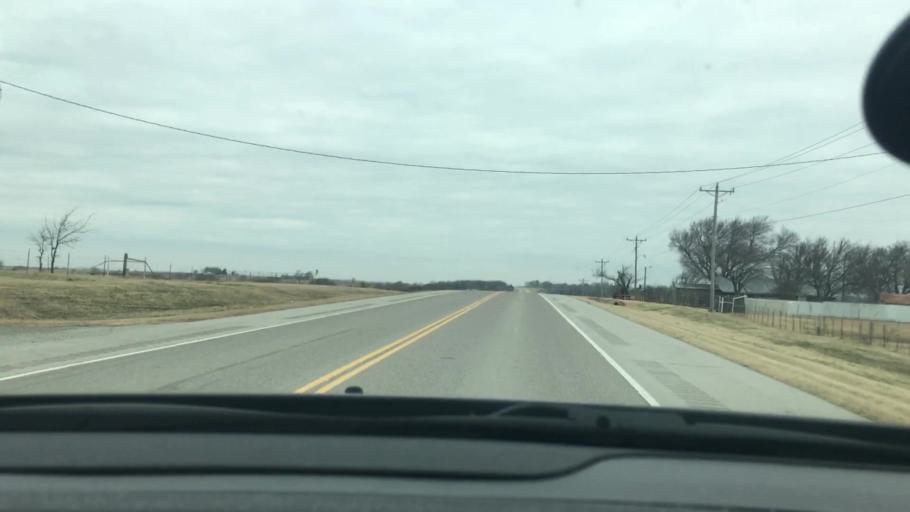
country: US
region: Oklahoma
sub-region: Garvin County
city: Wynnewood
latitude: 34.5141
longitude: -97.3359
